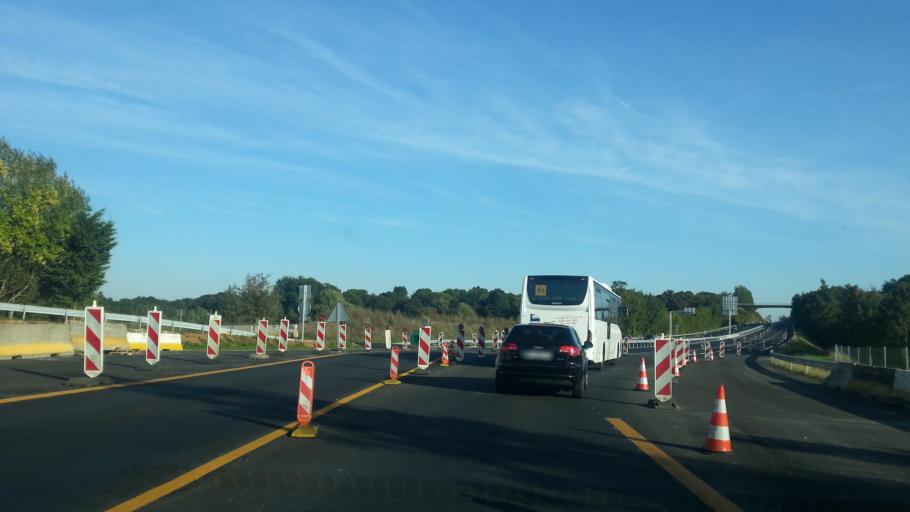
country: FR
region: Picardie
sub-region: Departement de l'Oise
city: Tille
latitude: 49.4596
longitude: 2.0883
